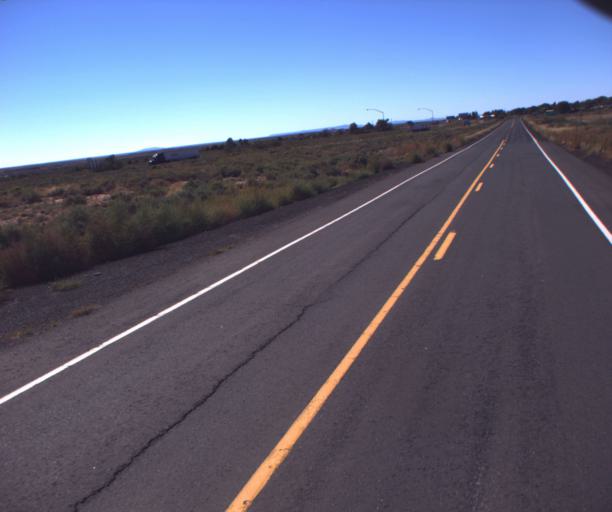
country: US
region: Arizona
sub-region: Navajo County
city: Joseph City
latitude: 34.9557
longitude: -110.3142
